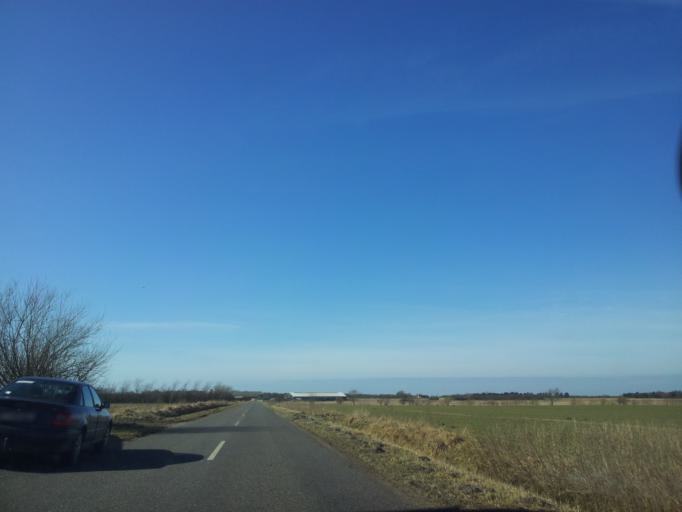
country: DK
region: South Denmark
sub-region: Tonder Kommune
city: Sherrebek
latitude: 55.1711
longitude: 8.7338
